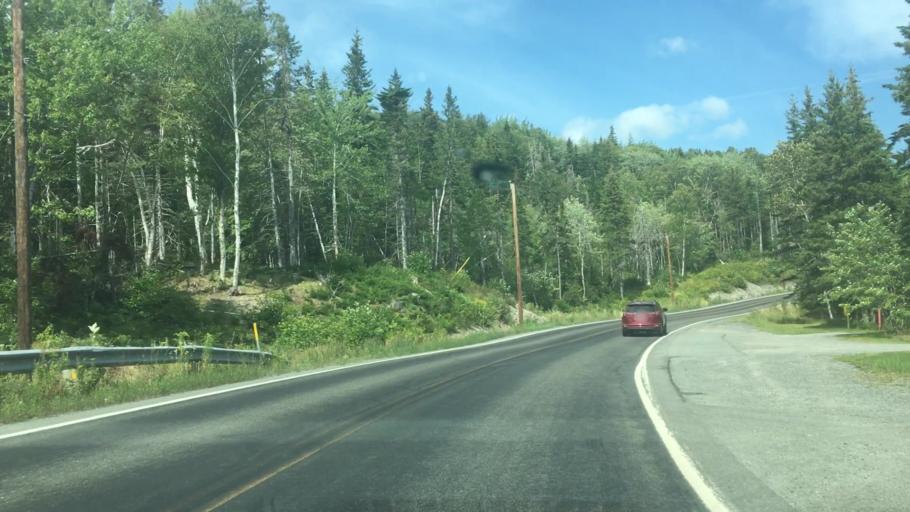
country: CA
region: Nova Scotia
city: Sydney Mines
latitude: 46.2064
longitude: -60.6224
